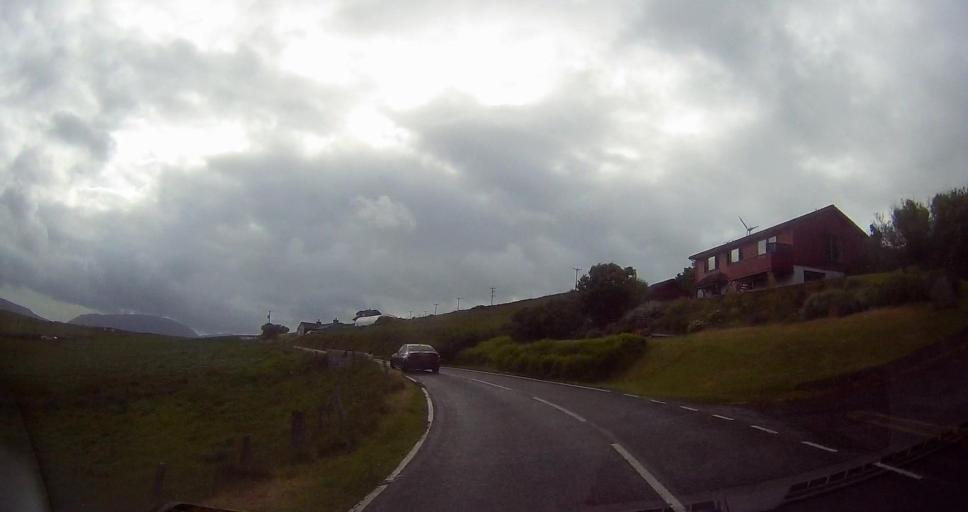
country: GB
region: Scotland
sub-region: Orkney Islands
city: Stromness
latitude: 58.9209
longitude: -3.1860
